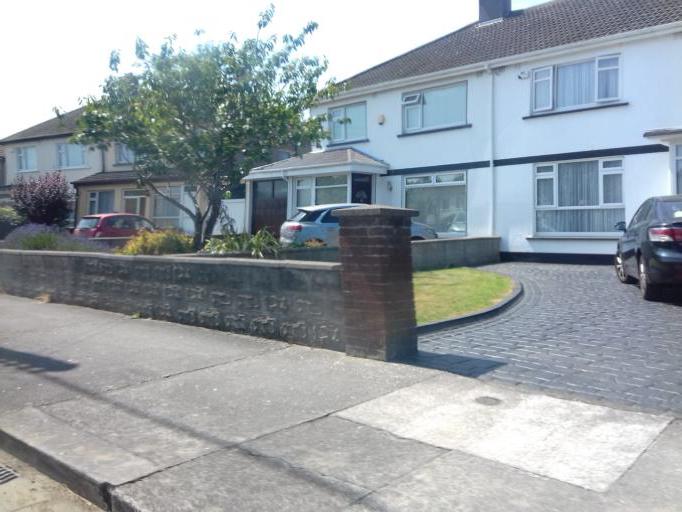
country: IE
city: Bayside
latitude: 53.3905
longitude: -6.1366
